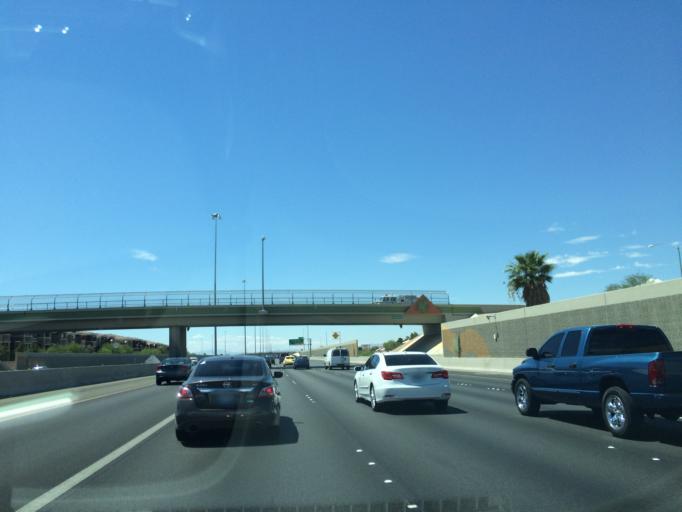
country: US
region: Nevada
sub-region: Clark County
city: Las Vegas
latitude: 36.2489
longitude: -115.2469
